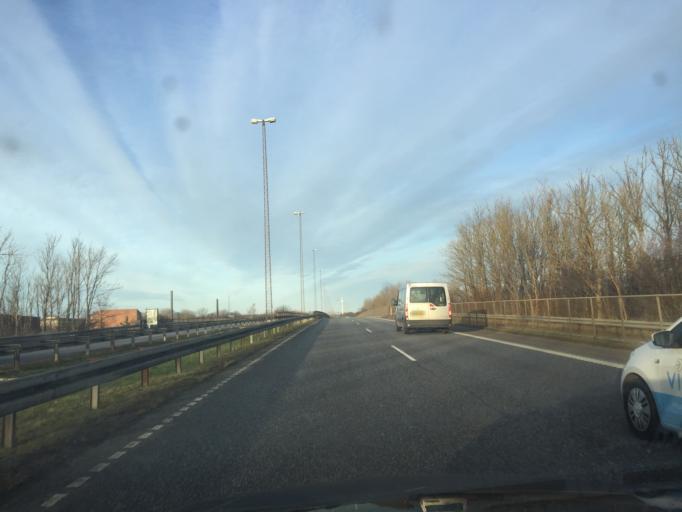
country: DK
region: Capital Region
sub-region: Hoje-Taastrup Kommune
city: Taastrup
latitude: 55.6488
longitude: 12.2823
